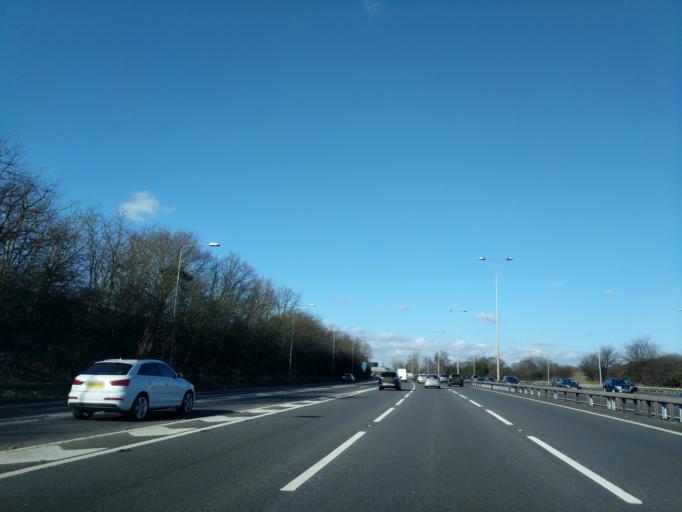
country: GB
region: England
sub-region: Surrey
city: Chertsey
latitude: 51.3791
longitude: -0.5119
